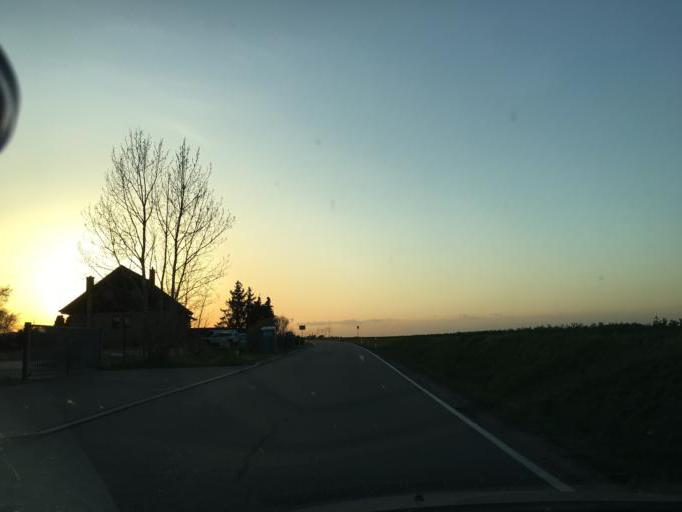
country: DE
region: Saxony
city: Grossbardau
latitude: 51.2062
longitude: 12.6930
